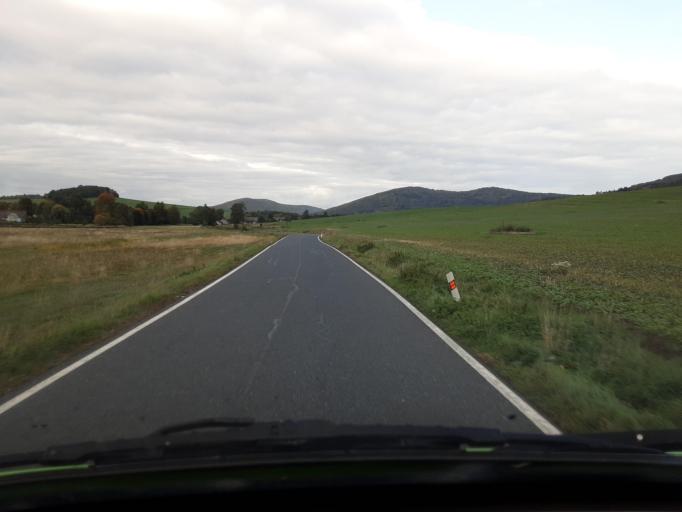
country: CZ
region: Plzensky
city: Janovice nad Uhlavou
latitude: 49.4079
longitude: 13.1586
